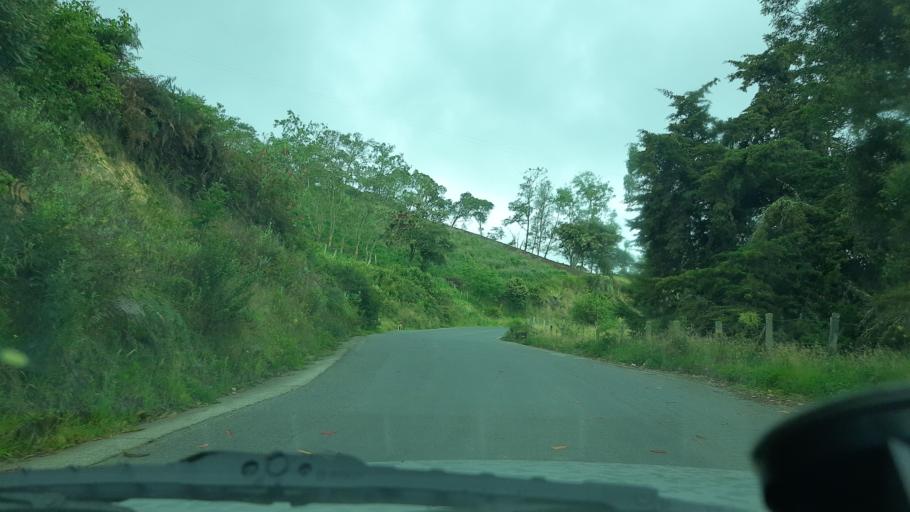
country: CO
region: Cundinamarca
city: Umbita
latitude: 5.2209
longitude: -73.4724
